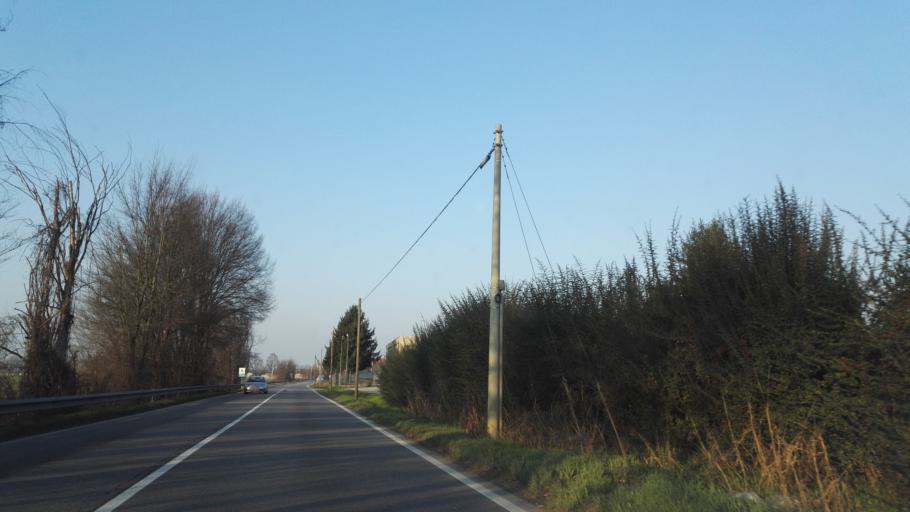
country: IT
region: Lombardy
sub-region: Citta metropolitana di Milano
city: Mombretto
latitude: 45.4071
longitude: 9.3577
